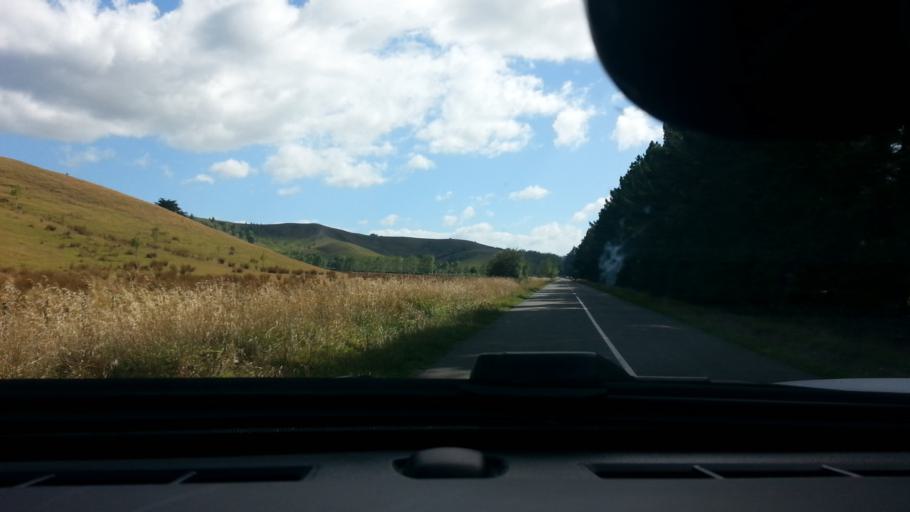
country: NZ
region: Wellington
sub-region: Masterton District
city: Masterton
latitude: -40.8883
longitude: 175.8440
